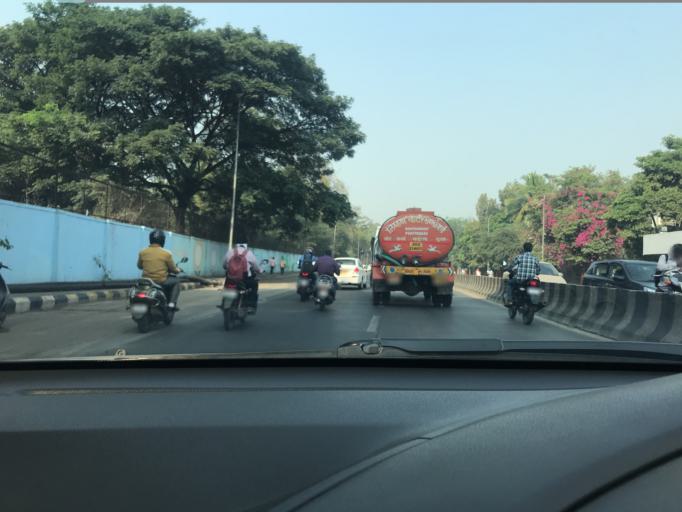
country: IN
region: Maharashtra
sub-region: Pune Division
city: Khadki
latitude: 18.5472
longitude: 73.8167
